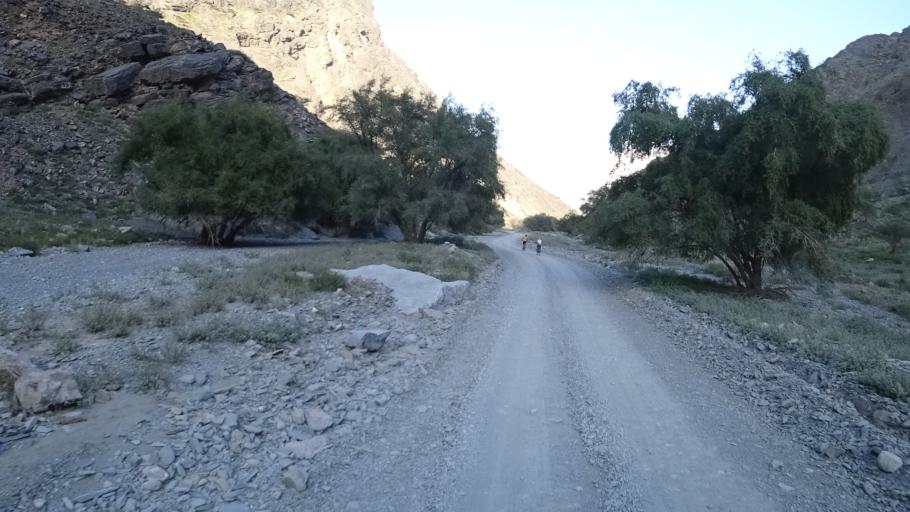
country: OM
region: Al Batinah
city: Bayt al `Awabi
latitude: 23.2541
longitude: 57.3991
